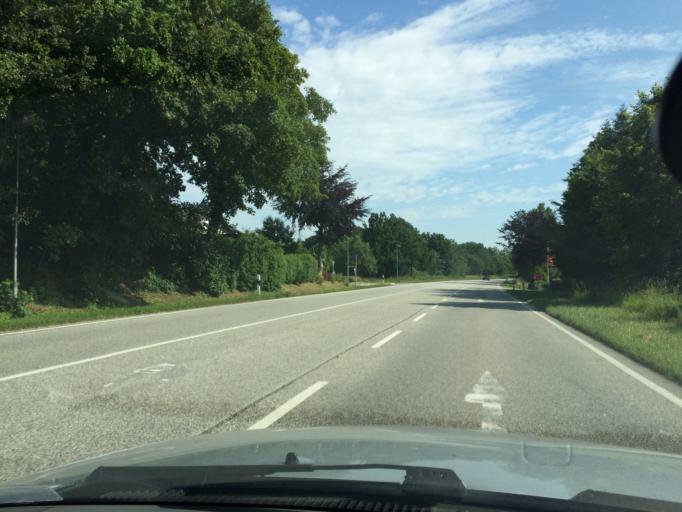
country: DE
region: Schleswig-Holstein
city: Sankelmark
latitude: 54.7238
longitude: 9.4427
